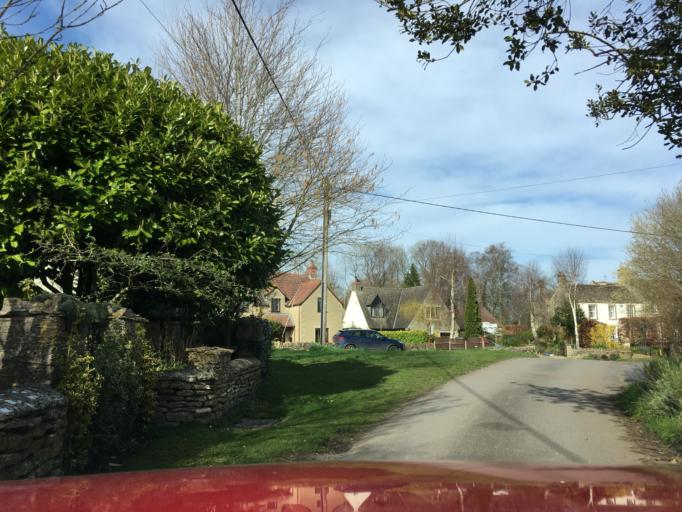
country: GB
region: England
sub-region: Wiltshire
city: Chippenham
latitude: 51.4892
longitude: -2.1182
